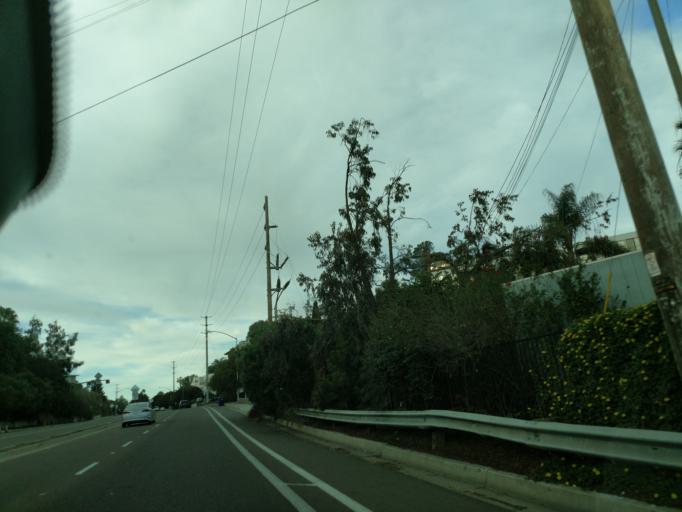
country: US
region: California
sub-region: San Diego County
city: Coronado
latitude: 32.7305
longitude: -117.2278
